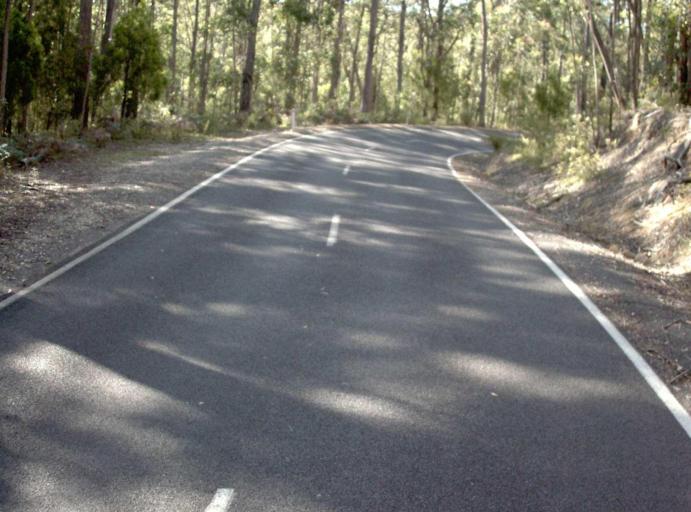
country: AU
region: Victoria
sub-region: East Gippsland
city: Lakes Entrance
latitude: -37.5851
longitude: 148.5356
